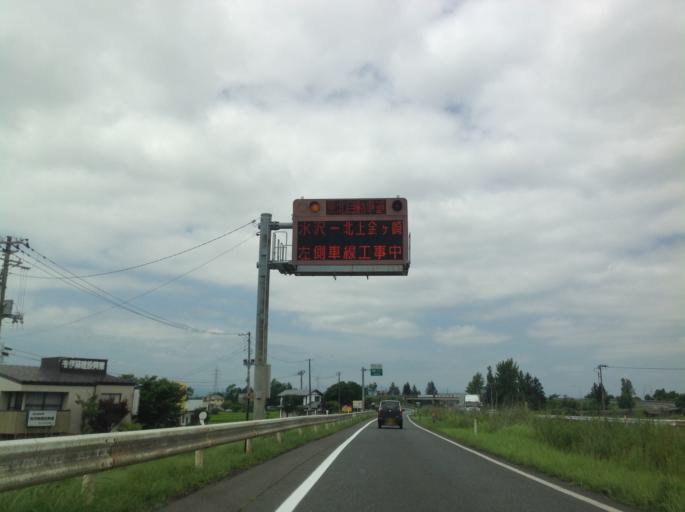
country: JP
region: Iwate
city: Mizusawa
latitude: 39.1700
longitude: 141.1259
